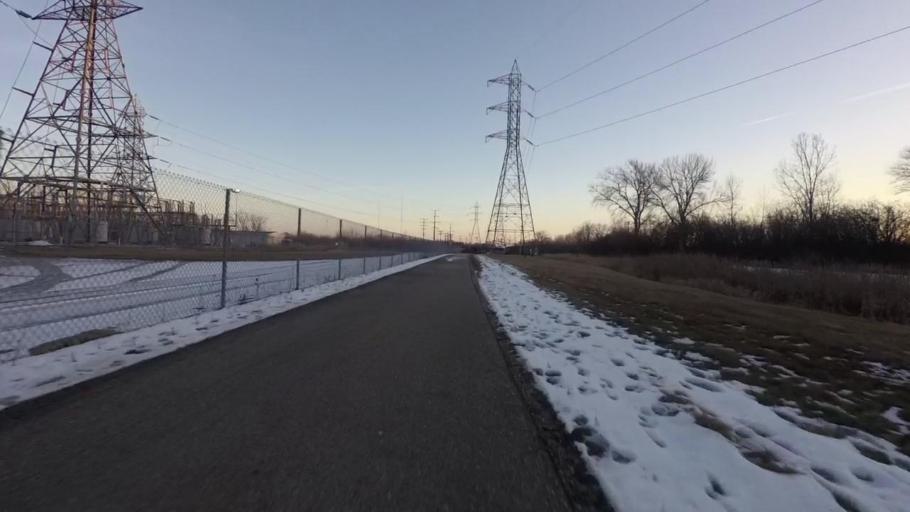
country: US
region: Wisconsin
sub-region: Milwaukee County
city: Glendale
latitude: 43.1322
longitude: -87.9474
